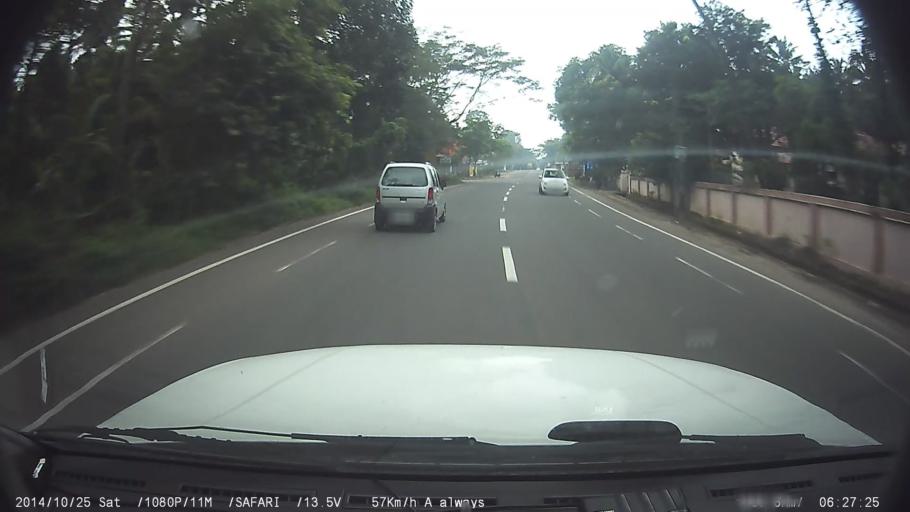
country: IN
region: Kerala
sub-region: Ernakulam
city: Perumbavoor
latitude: 10.0553
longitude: 76.5304
